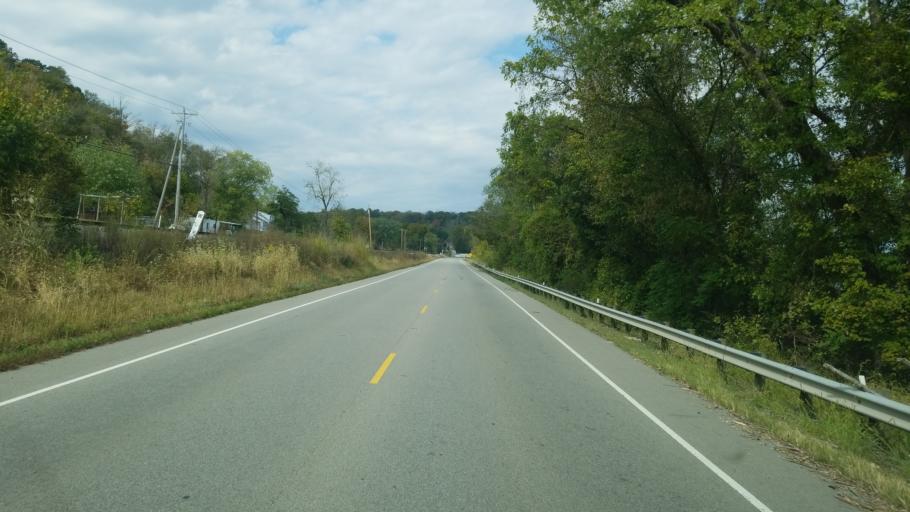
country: US
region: West Virginia
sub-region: Mason County
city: Point Pleasant
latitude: 38.8786
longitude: -82.1444
